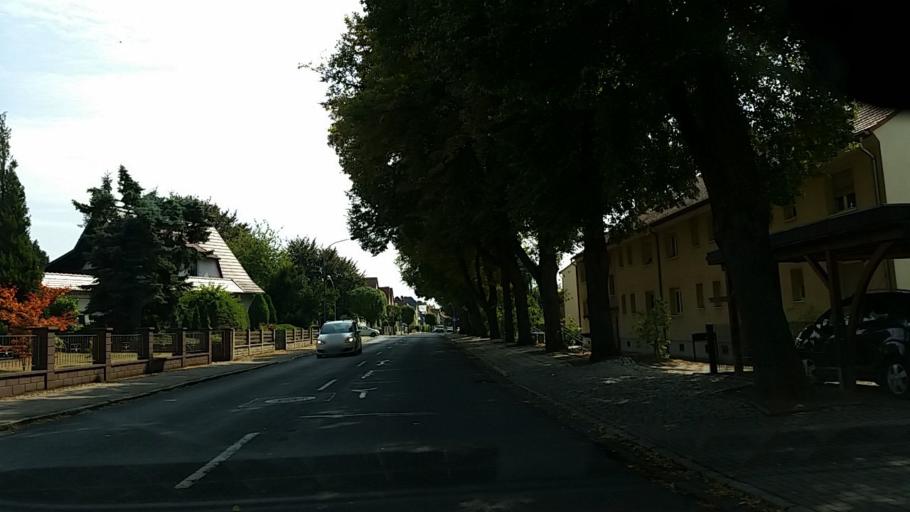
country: DE
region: Thuringia
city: Artern
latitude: 51.3707
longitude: 11.2894
